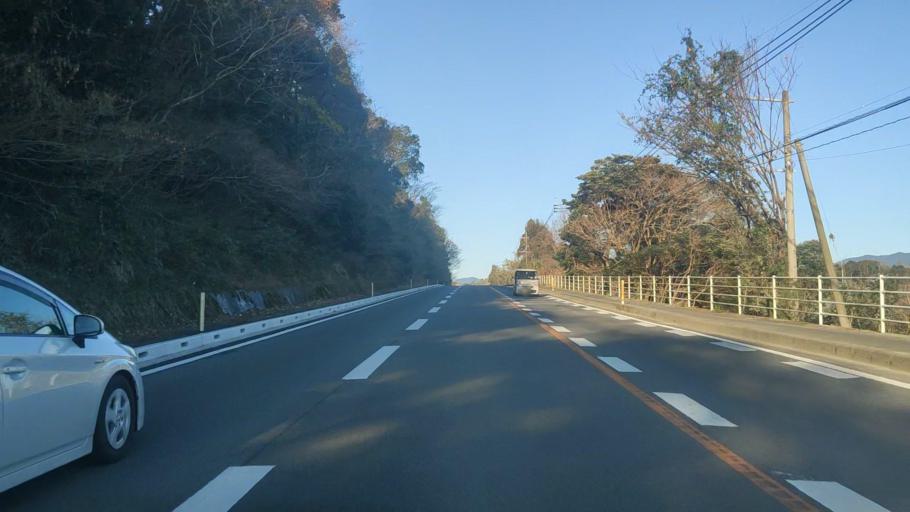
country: JP
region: Miyazaki
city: Takanabe
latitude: 32.1519
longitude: 131.5228
